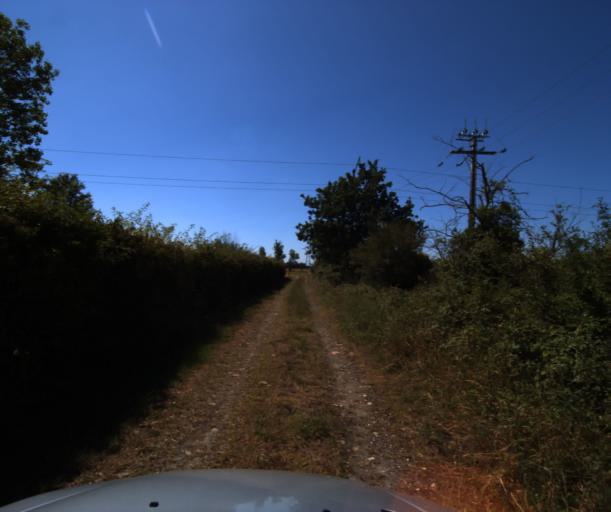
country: FR
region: Midi-Pyrenees
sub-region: Departement de la Haute-Garonne
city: Muret
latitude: 43.4558
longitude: 1.3676
